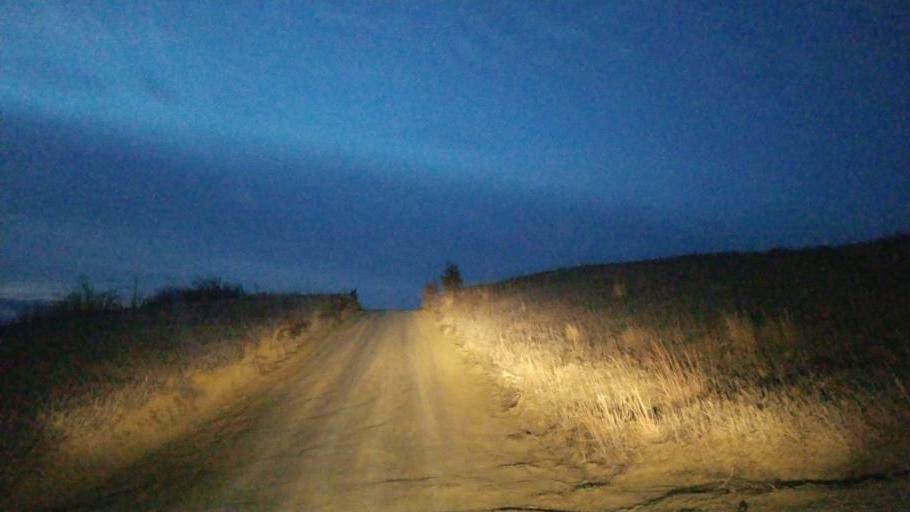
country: US
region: Nebraska
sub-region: Knox County
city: Center
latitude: 42.5681
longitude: -97.7985
